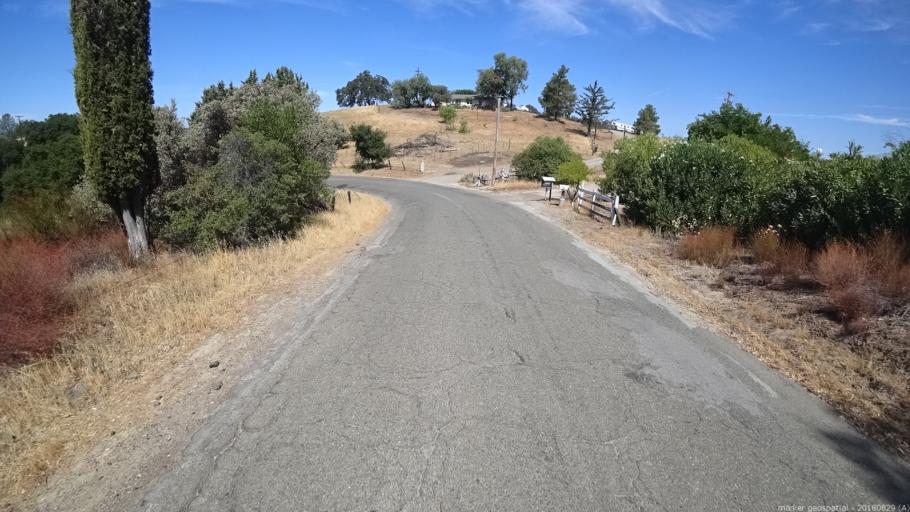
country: US
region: California
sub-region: San Luis Obispo County
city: Lake Nacimiento
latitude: 35.8229
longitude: -121.0577
